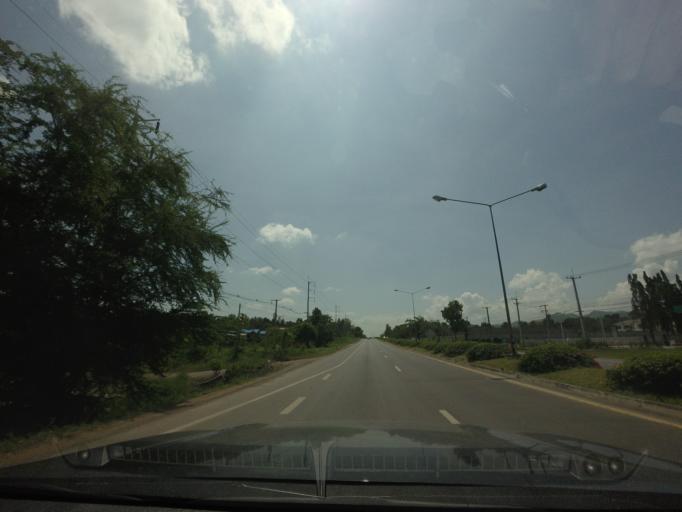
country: TH
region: Phetchabun
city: Lom Sak
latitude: 16.6776
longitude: 101.1615
